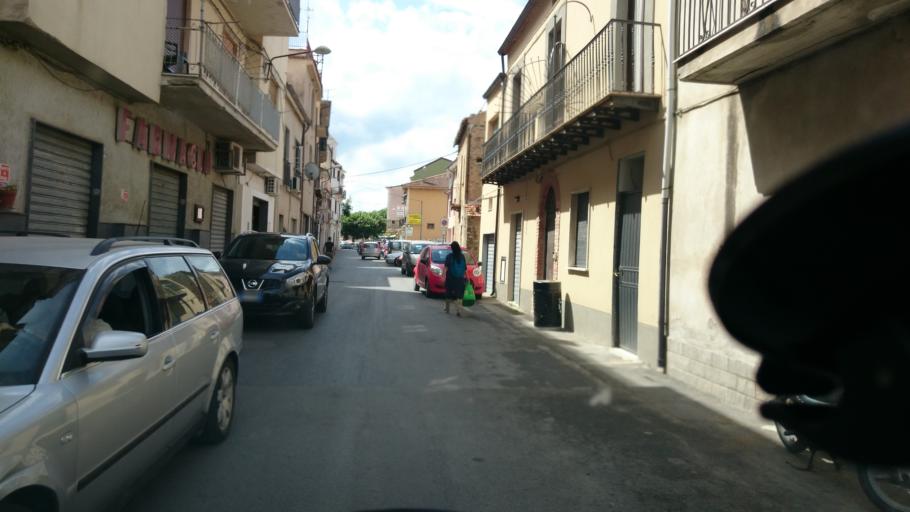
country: IT
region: Campania
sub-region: Provincia di Salerno
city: Pisciotta
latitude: 40.1100
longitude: 15.2332
